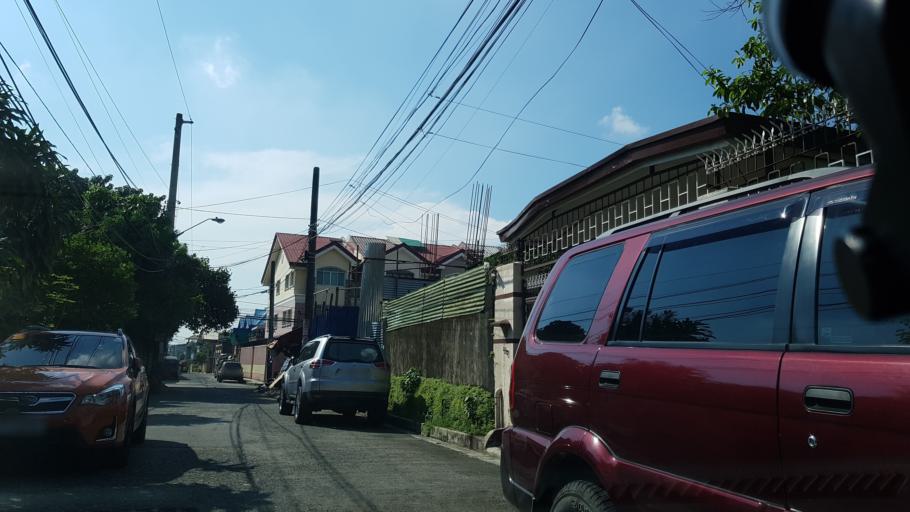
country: PH
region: Metro Manila
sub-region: Quezon City
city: Quezon City
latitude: 14.6252
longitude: 121.0440
